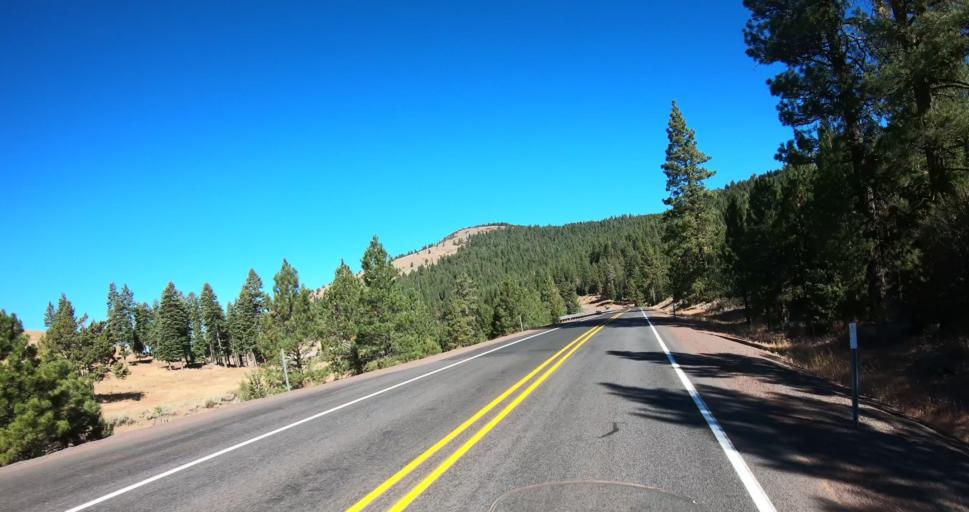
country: US
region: Oregon
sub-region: Lake County
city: Lakeview
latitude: 42.2342
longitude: -120.2922
